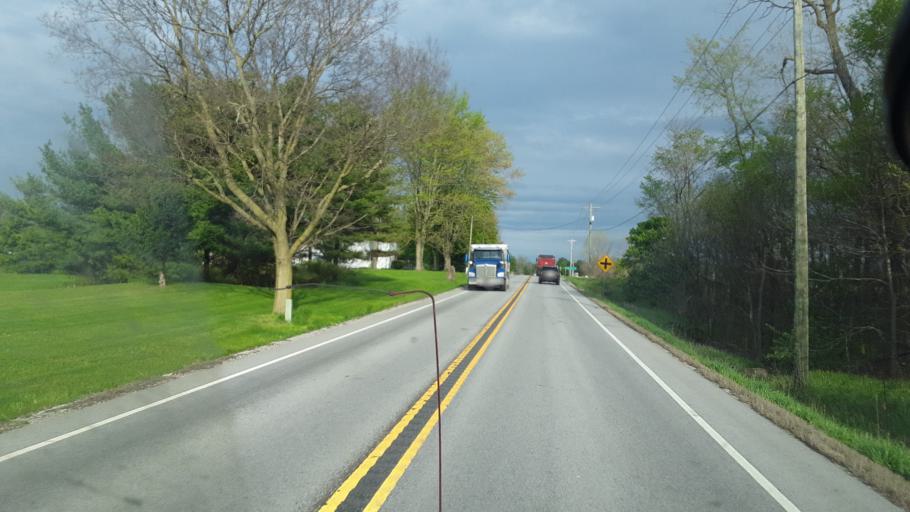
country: US
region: Indiana
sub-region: Whitley County
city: Churubusco
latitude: 41.2566
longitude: -85.3627
